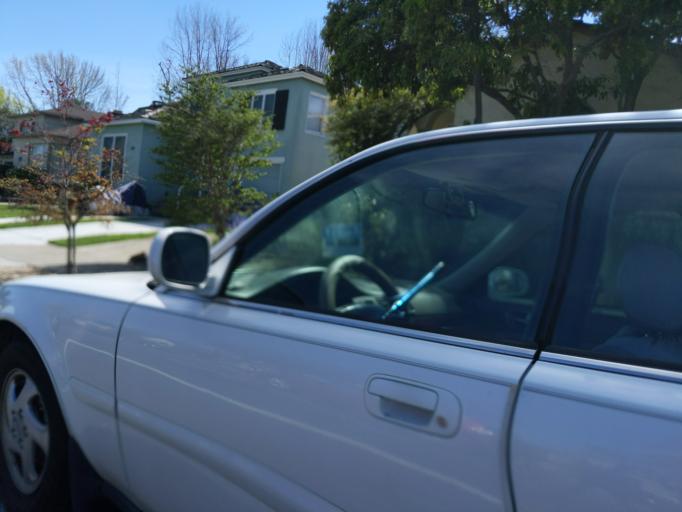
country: US
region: California
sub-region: Alameda County
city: Alameda
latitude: 37.7640
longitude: -122.2272
